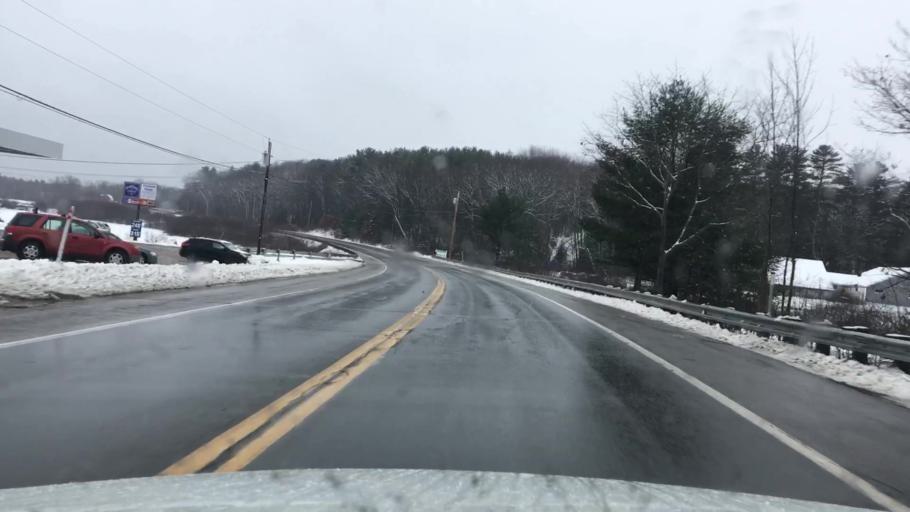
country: US
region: Maine
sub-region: Knox County
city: Rockport
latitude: 44.1776
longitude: -69.1489
